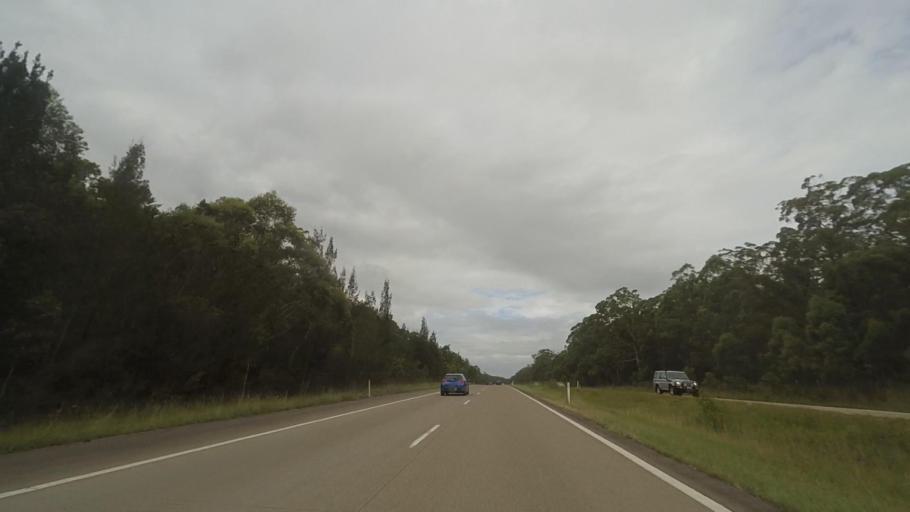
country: AU
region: New South Wales
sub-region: Port Stephens Shire
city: Medowie
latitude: -32.6513
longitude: 151.8928
